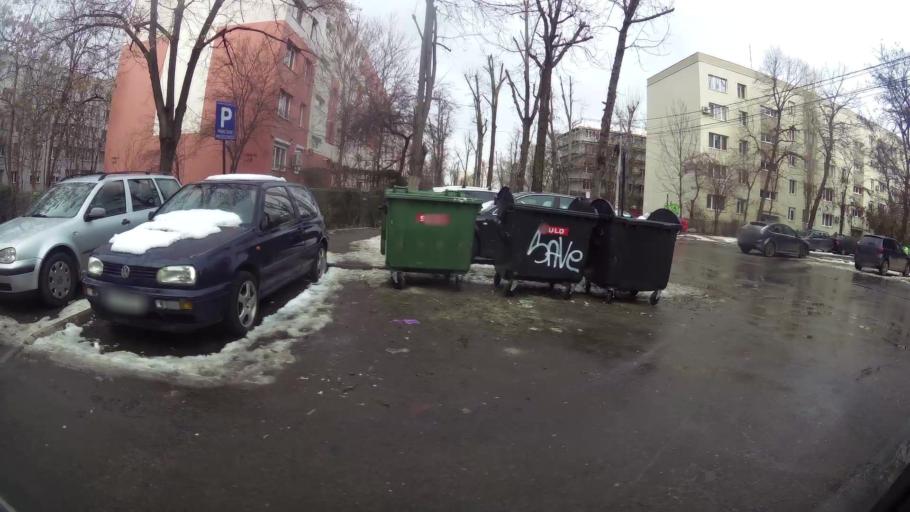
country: RO
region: Ilfov
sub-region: Comuna Popesti-Leordeni
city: Popesti-Leordeni
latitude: 44.4060
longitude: 26.1763
